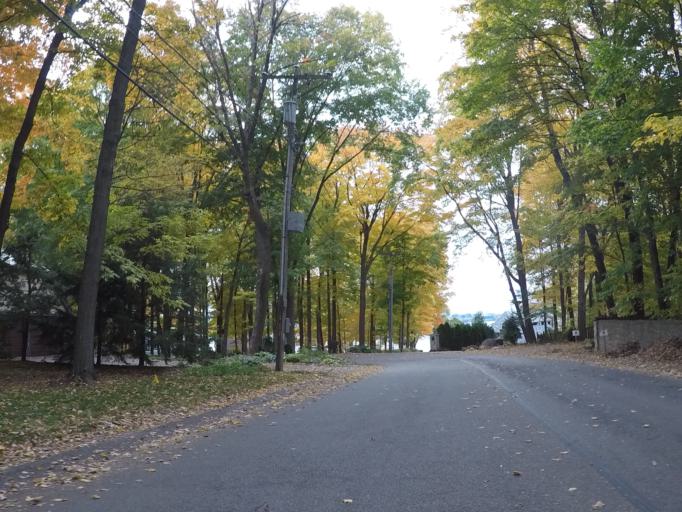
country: US
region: Wisconsin
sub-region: Dane County
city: Maple Bluff
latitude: 43.1151
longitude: -89.3809
